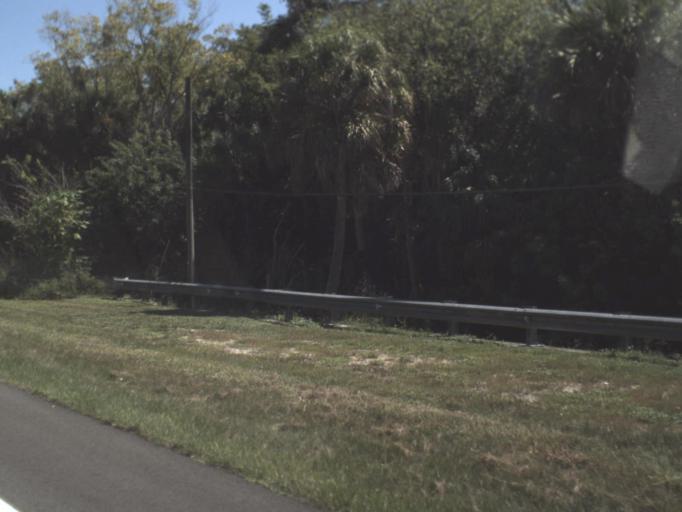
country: US
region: Florida
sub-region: Glades County
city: Moore Haven
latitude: 27.0084
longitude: -81.0412
